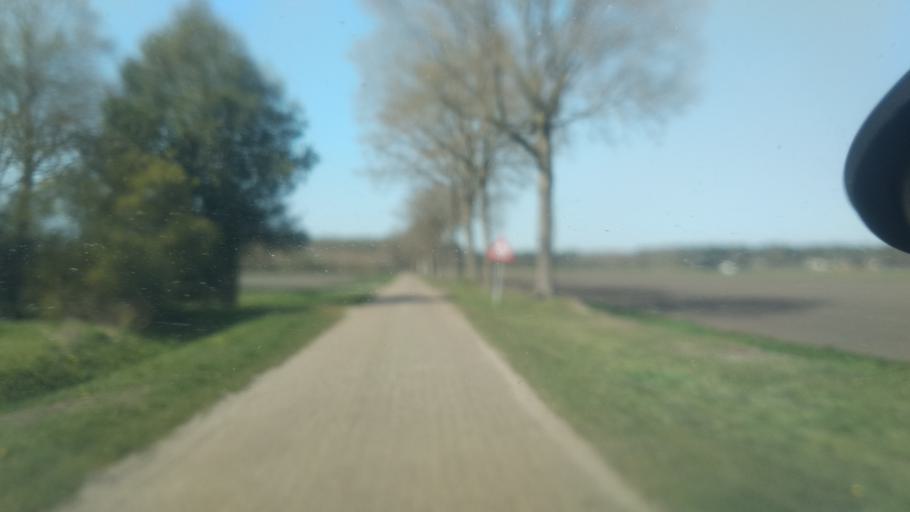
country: NL
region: Drenthe
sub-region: Gemeente Borger-Odoorn
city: Borger
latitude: 52.9245
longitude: 6.7371
